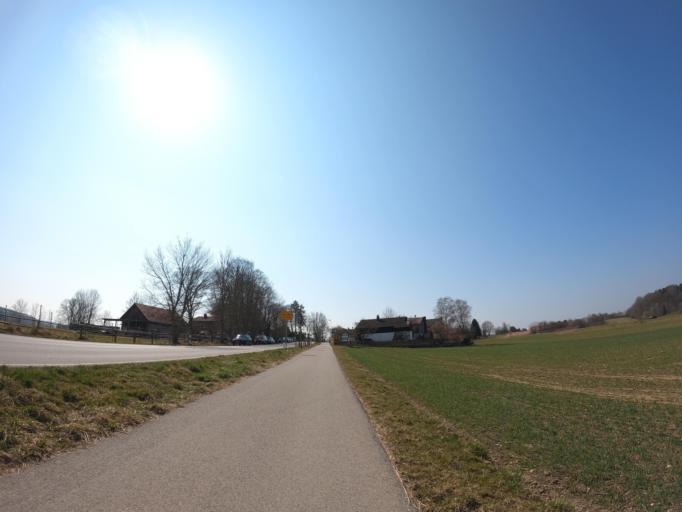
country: DE
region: Bavaria
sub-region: Upper Bavaria
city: Schaftlarn
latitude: 48.0152
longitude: 11.4100
